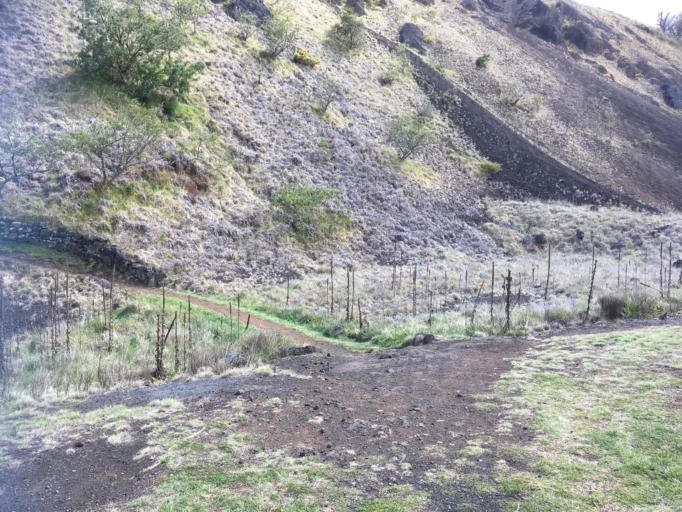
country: US
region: Hawaii
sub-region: Hawaii County
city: Volcano
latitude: 19.6881
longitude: -155.4668
